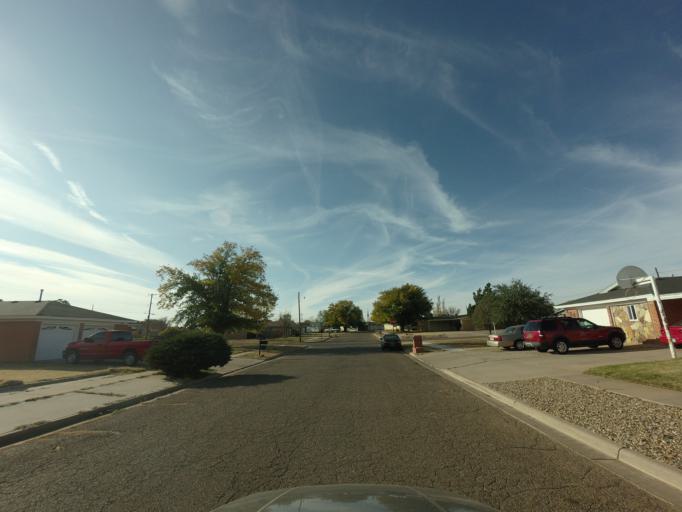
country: US
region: New Mexico
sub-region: Curry County
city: Clovis
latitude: 34.4244
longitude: -103.2233
